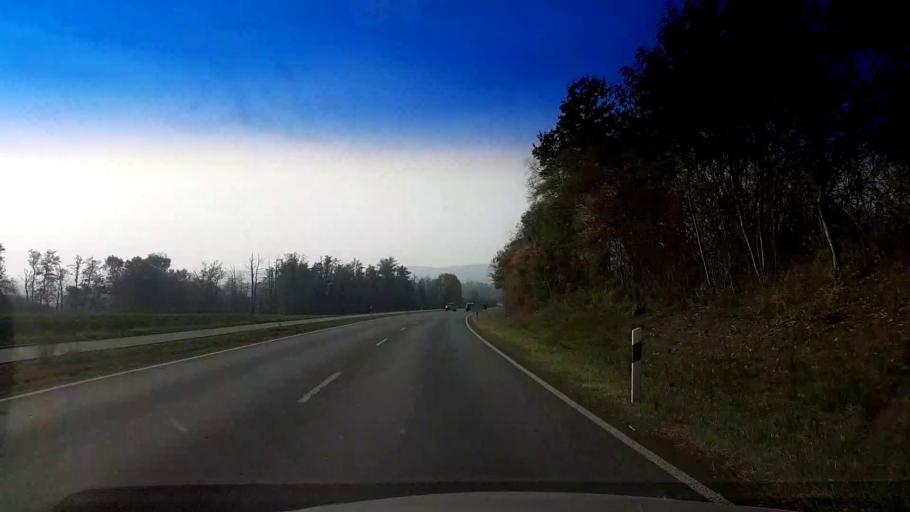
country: DE
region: Bavaria
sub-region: Upper Franconia
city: Himmelkron
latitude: 50.0730
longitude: 11.6089
